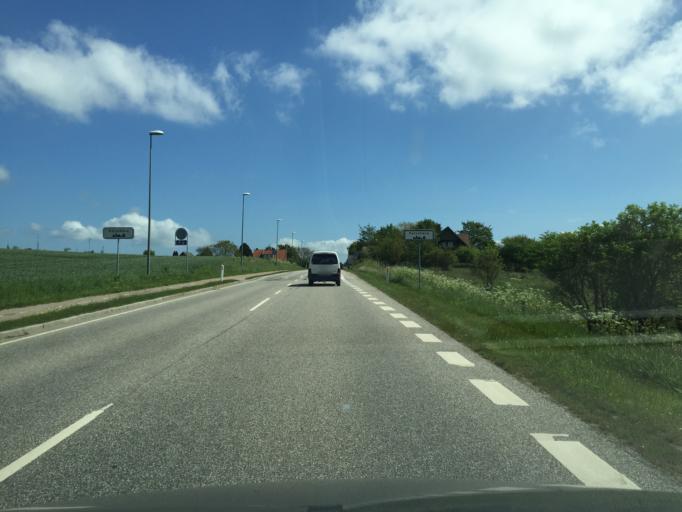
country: DK
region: Zealand
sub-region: Vordingborg Kommune
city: Stege
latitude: 54.9969
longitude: 12.1512
